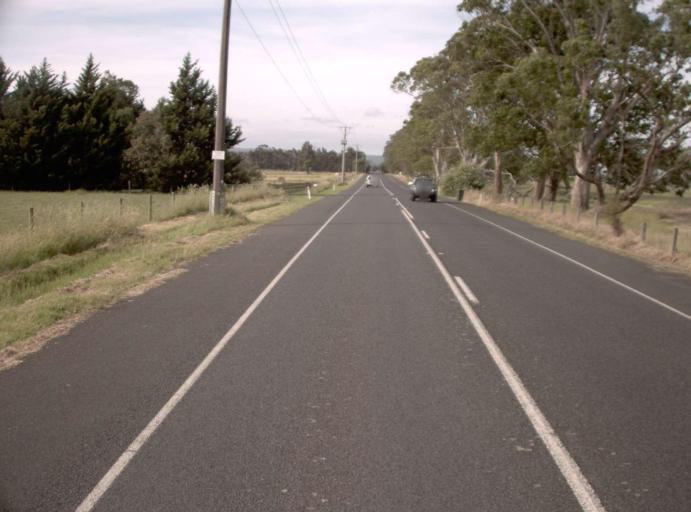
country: AU
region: Victoria
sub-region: Latrobe
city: Traralgon
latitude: -38.1455
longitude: 146.5556
